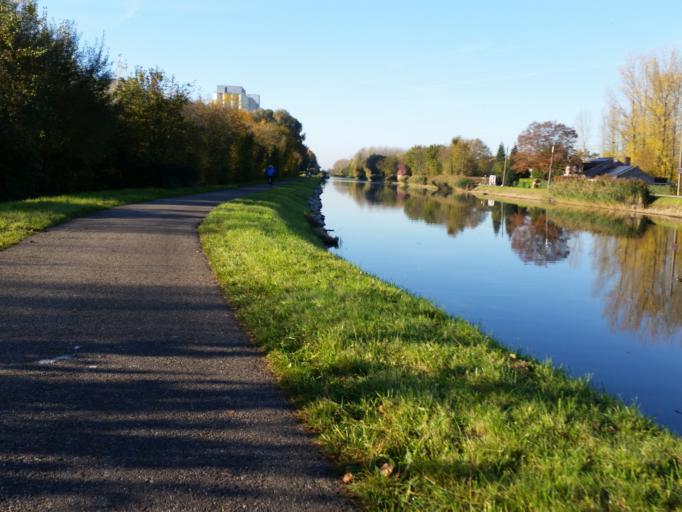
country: BE
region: Flanders
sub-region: Provincie Vlaams-Brabant
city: Herent
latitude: 50.9265
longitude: 4.6852
